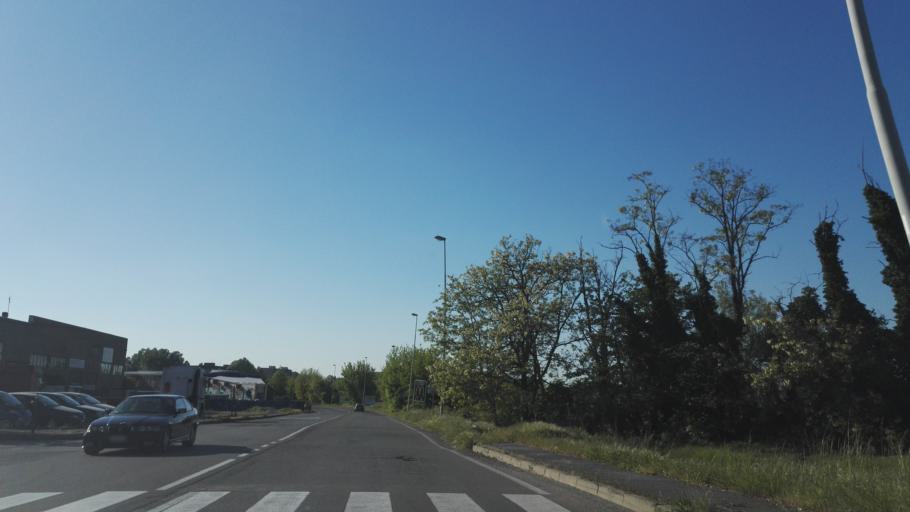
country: IT
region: Lombardy
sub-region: Citta metropolitana di Milano
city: San Giuliano Milanese
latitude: 45.3960
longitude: 9.2965
